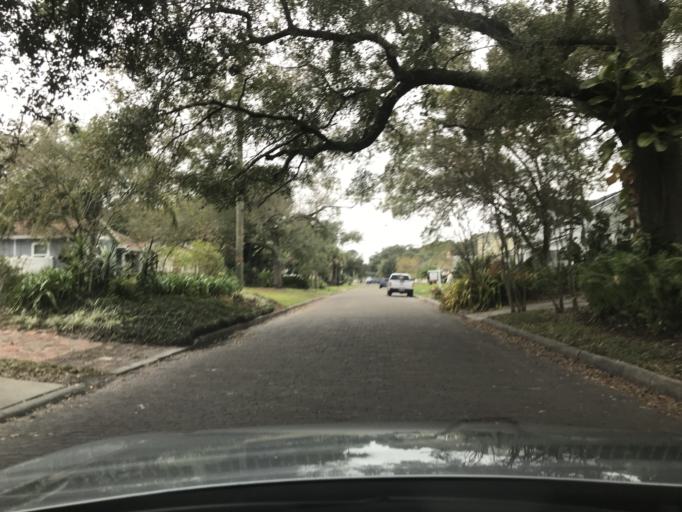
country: US
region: Florida
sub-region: Hillsborough County
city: Tampa
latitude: 27.9763
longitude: -82.4720
